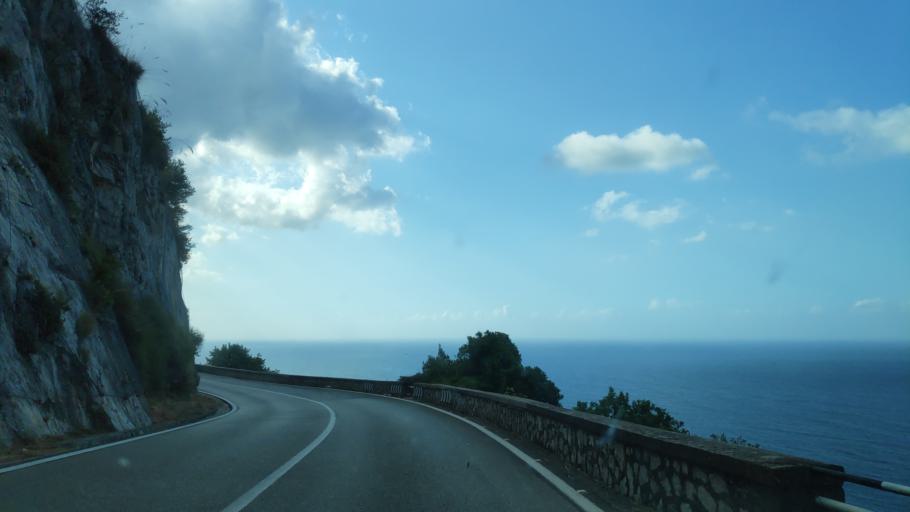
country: IT
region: Campania
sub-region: Provincia di Napoli
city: Arola-Preazzano
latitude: 40.6212
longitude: 14.4550
